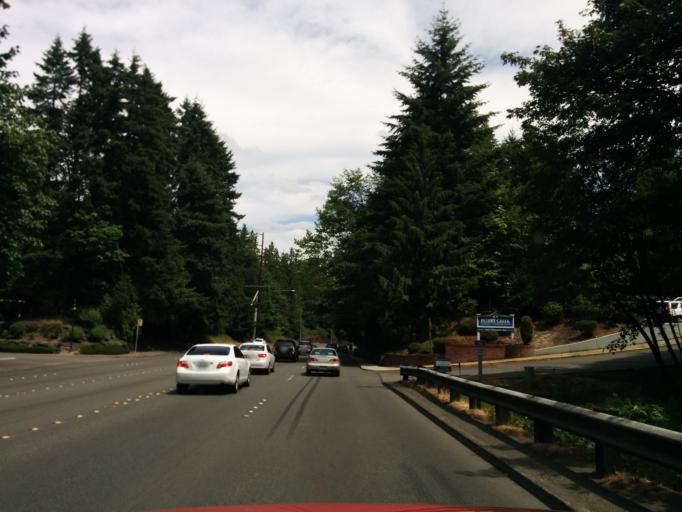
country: US
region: Washington
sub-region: King County
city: Redmond
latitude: 47.6747
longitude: -122.1474
